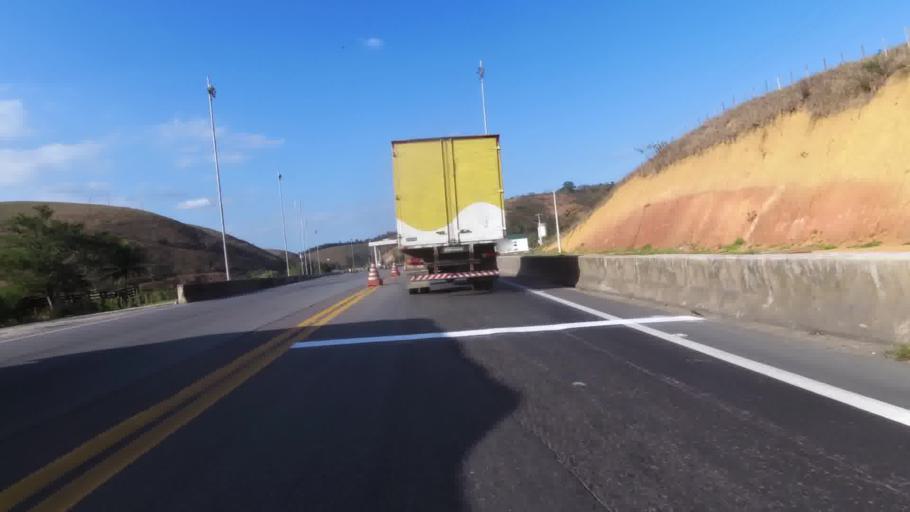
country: BR
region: Espirito Santo
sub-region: Mimoso Do Sul
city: Mimoso do Sul
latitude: -21.1594
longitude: -41.2822
